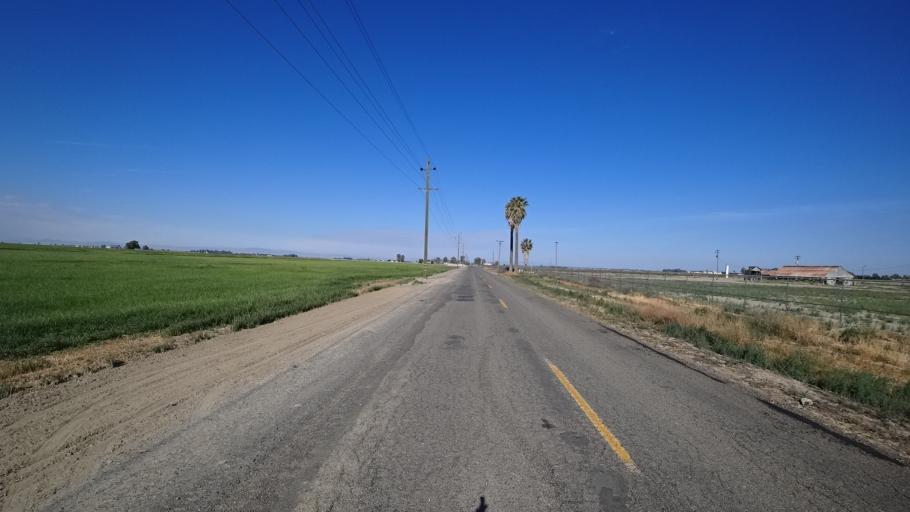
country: US
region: California
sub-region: Kings County
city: Stratford
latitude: 36.2256
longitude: -119.7530
